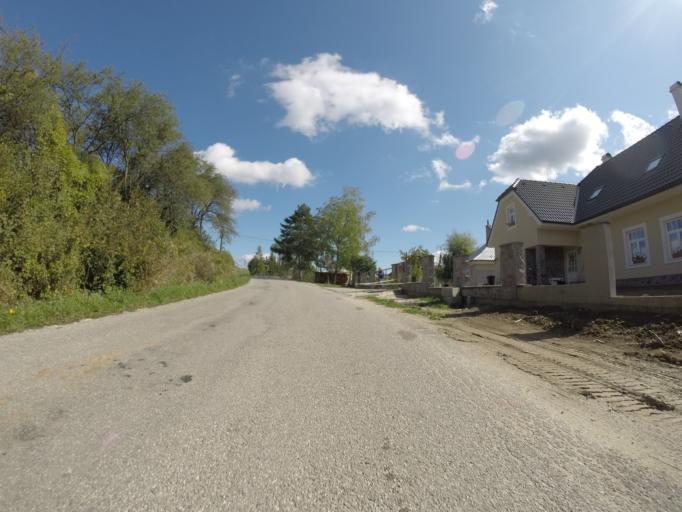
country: SK
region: Nitriansky
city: Stara Tura
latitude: 48.8346
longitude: 17.7448
